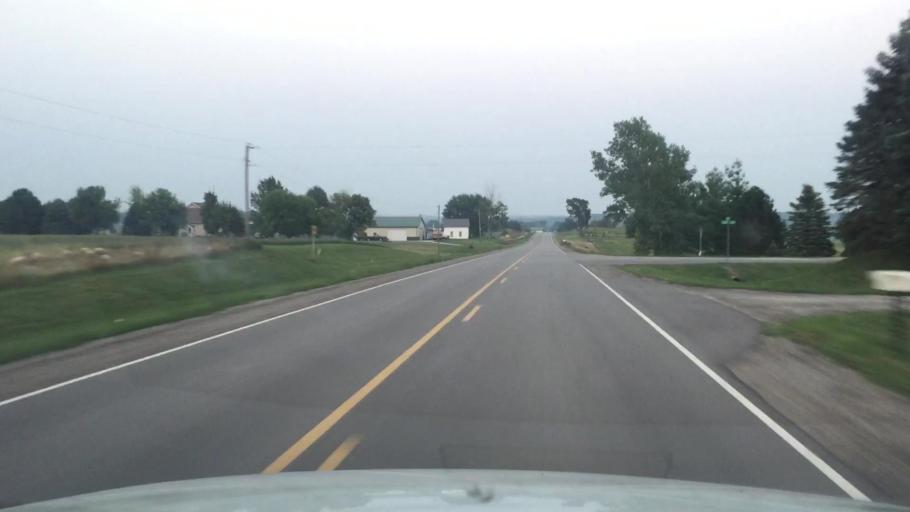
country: US
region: Iowa
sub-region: Marion County
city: Melcher-Dallas
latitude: 41.1897
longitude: -93.4052
